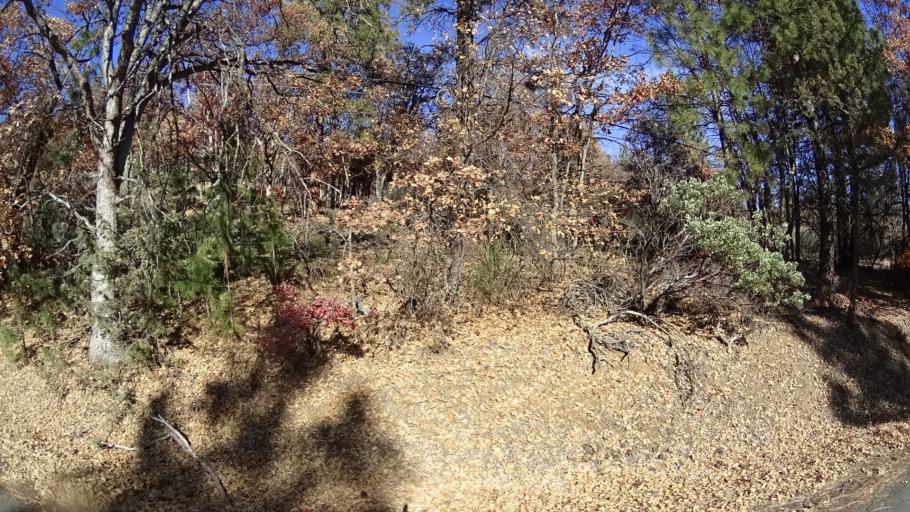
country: US
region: California
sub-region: Siskiyou County
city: Yreka
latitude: 41.7183
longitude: -122.6771
